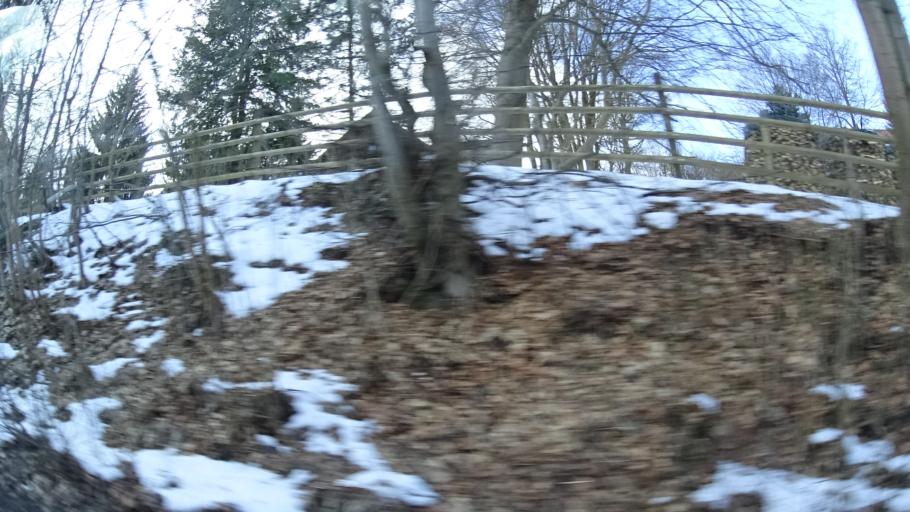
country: DE
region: Thuringia
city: Suhl
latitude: 50.6111
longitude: 10.6747
